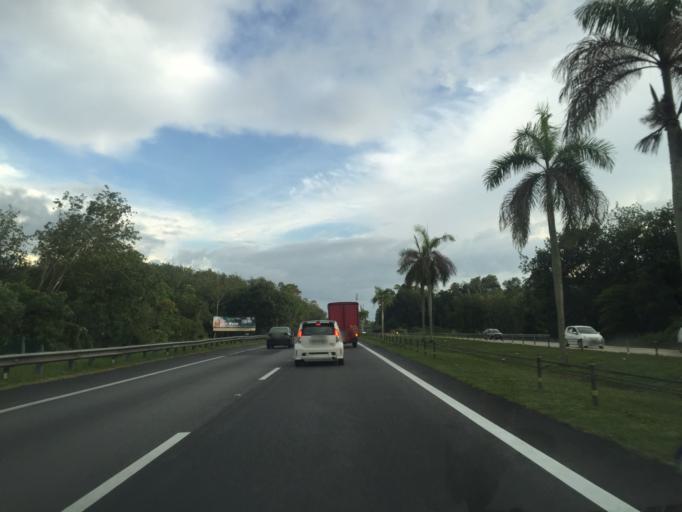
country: MY
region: Kedah
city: Gurun
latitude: 5.8579
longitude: 100.4810
